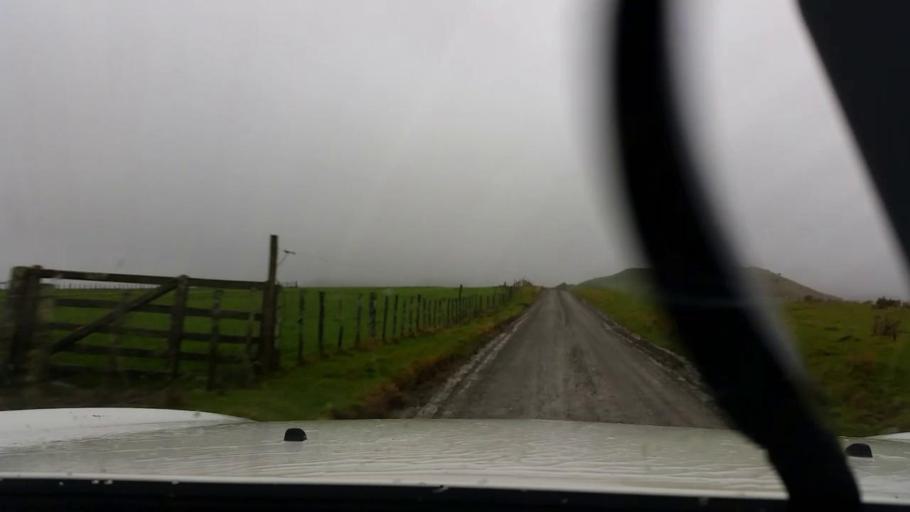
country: NZ
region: Wellington
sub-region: Masterton District
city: Masterton
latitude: -41.2507
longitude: 175.8947
